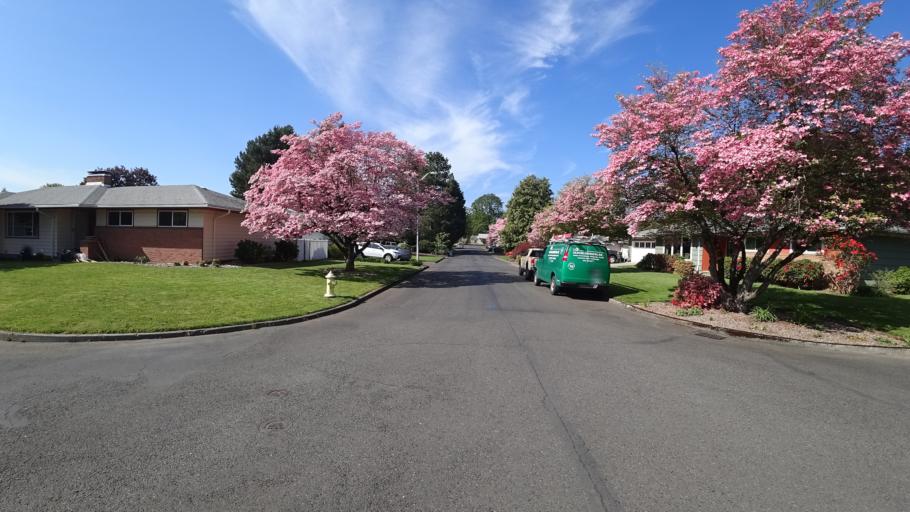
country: US
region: Oregon
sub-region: Clackamas County
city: Milwaukie
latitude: 45.4601
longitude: -122.6281
